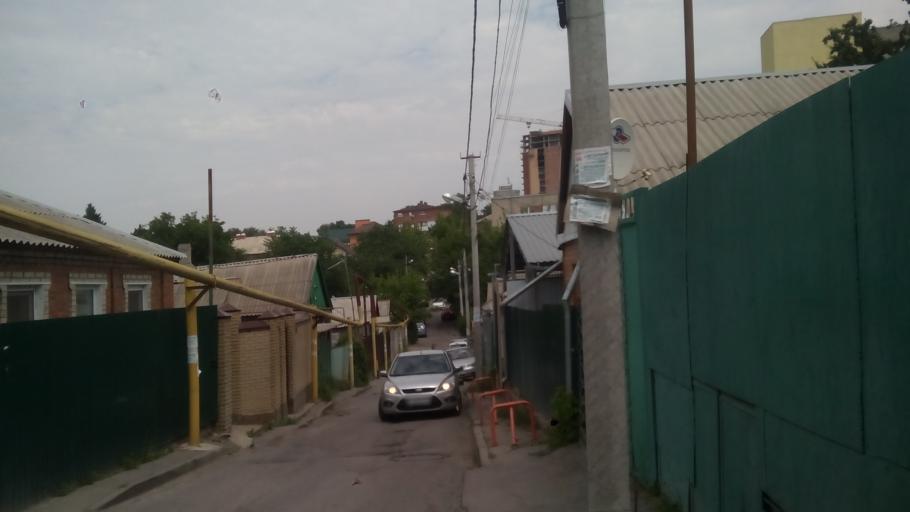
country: RU
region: Rostov
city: Rostov-na-Donu
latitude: 47.2466
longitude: 39.7426
